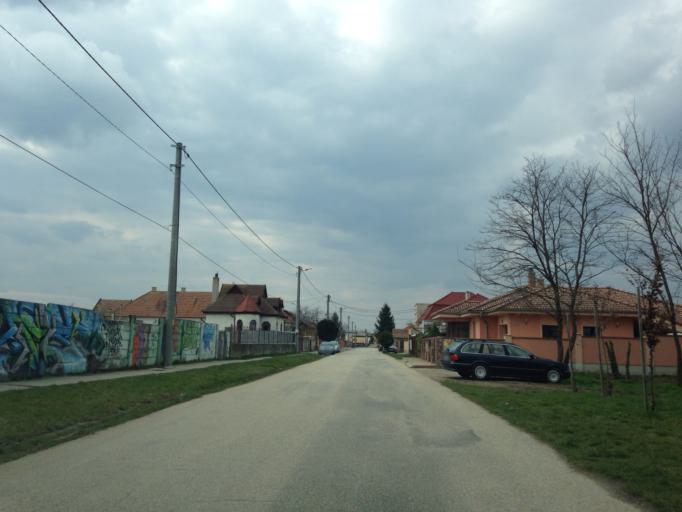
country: SK
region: Nitriansky
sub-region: Okres Nove Zamky
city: Nove Zamky
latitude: 47.9952
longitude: 18.2693
